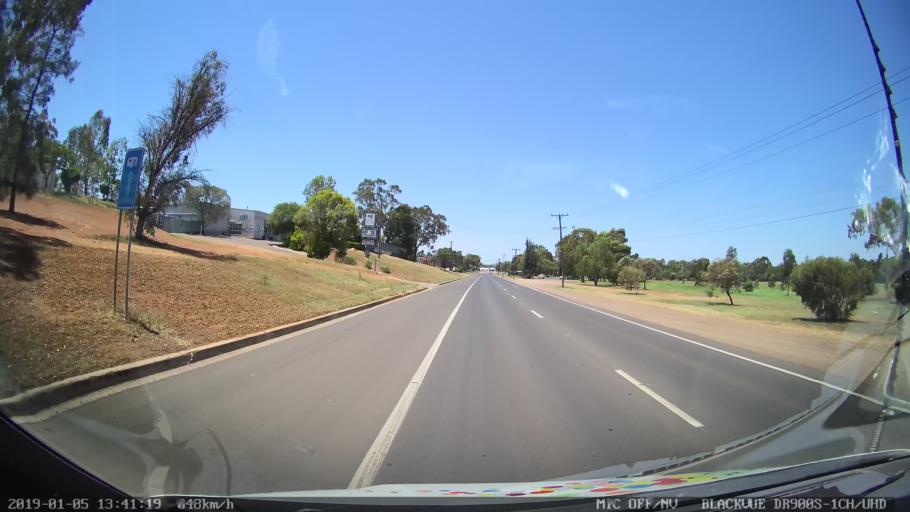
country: AU
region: New South Wales
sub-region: Gunnedah
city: Gunnedah
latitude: -30.9791
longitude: 150.2382
